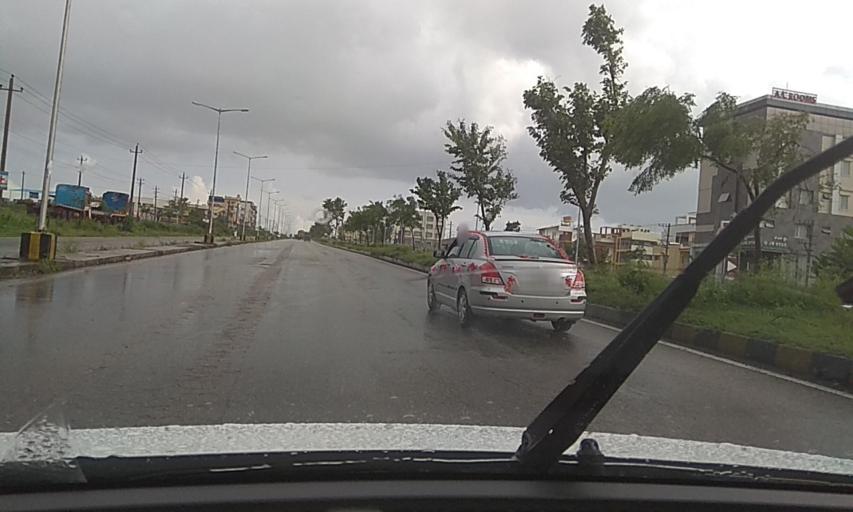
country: IN
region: Karnataka
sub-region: Mysore
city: Mysore
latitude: 12.3138
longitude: 76.7017
